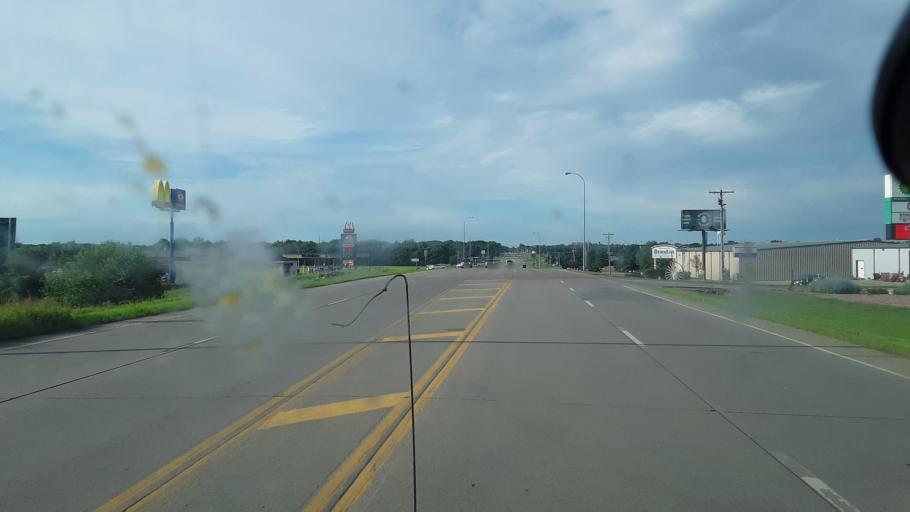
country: US
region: South Dakota
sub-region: Minnehaha County
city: Brandon
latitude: 43.6067
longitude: -96.5722
